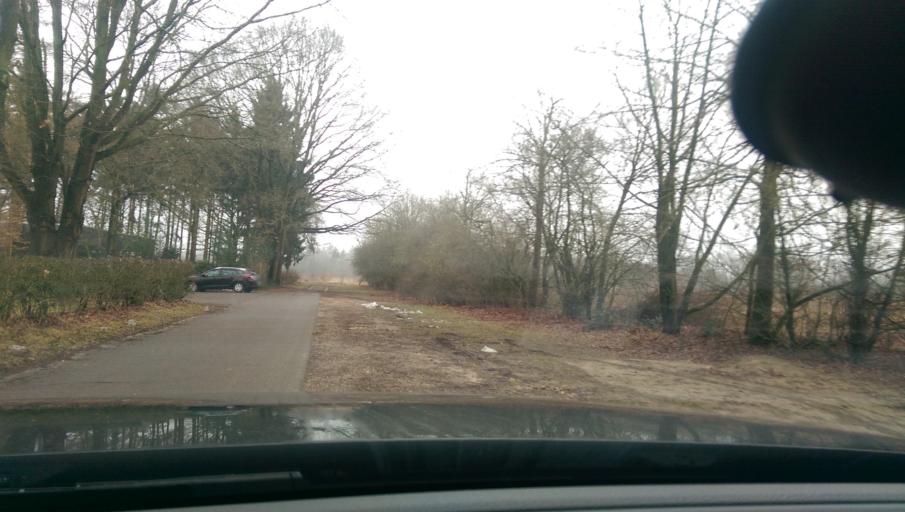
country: DE
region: Lower Saxony
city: Lindwedel
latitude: 52.5593
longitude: 9.6821
